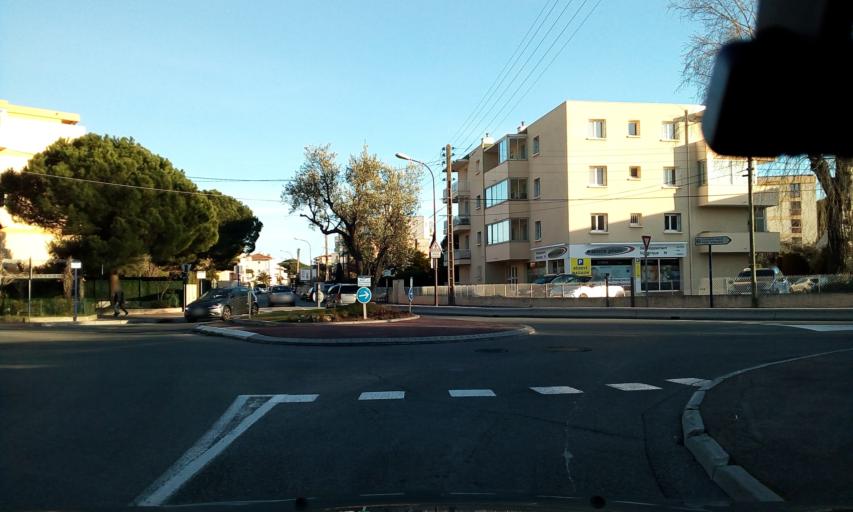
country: FR
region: Provence-Alpes-Cote d'Azur
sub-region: Departement du Var
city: Frejus
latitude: 43.4262
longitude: 6.7481
